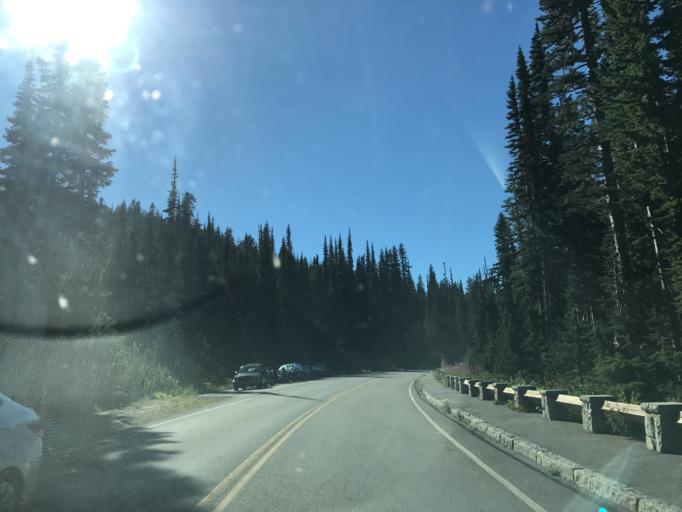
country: US
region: Washington
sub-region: Pierce County
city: Buckley
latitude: 46.7680
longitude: -121.7290
